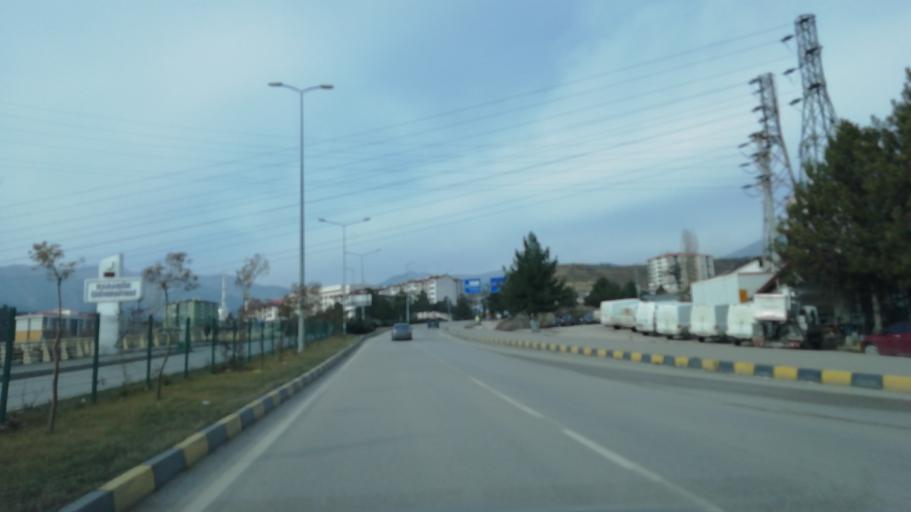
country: TR
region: Karabuk
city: Karabuk
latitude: 41.2174
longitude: 32.6543
